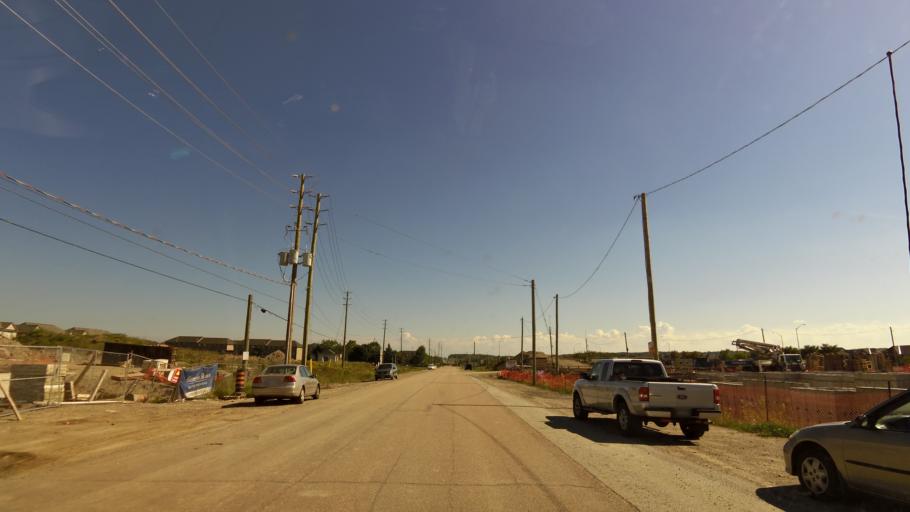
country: CA
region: Ontario
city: Burlington
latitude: 43.4323
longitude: -79.7718
